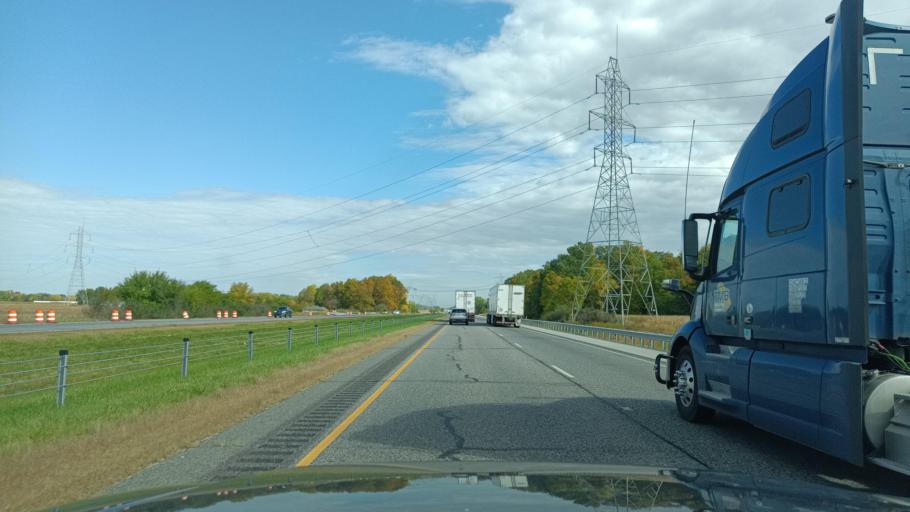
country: US
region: Indiana
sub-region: Huntington County
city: Roanoke
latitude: 40.9105
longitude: -85.3305
